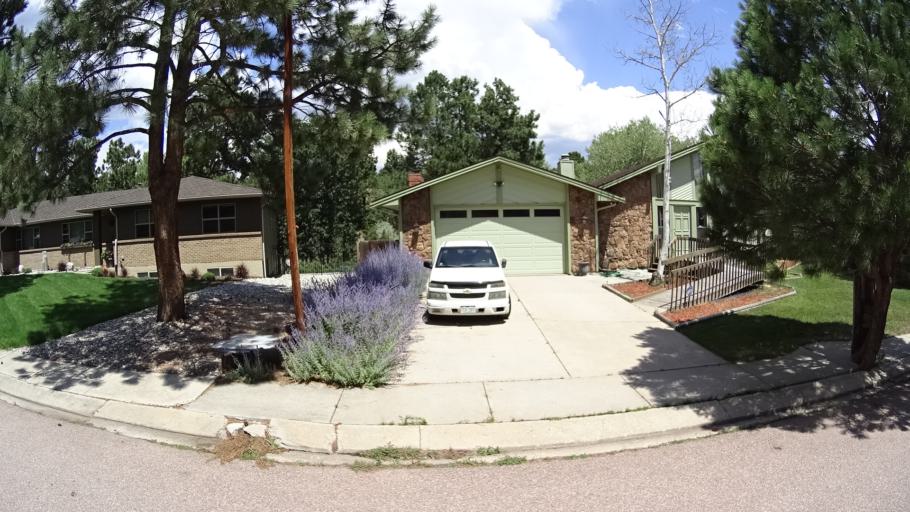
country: US
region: Colorado
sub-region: El Paso County
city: Air Force Academy
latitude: 38.9364
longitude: -104.8359
